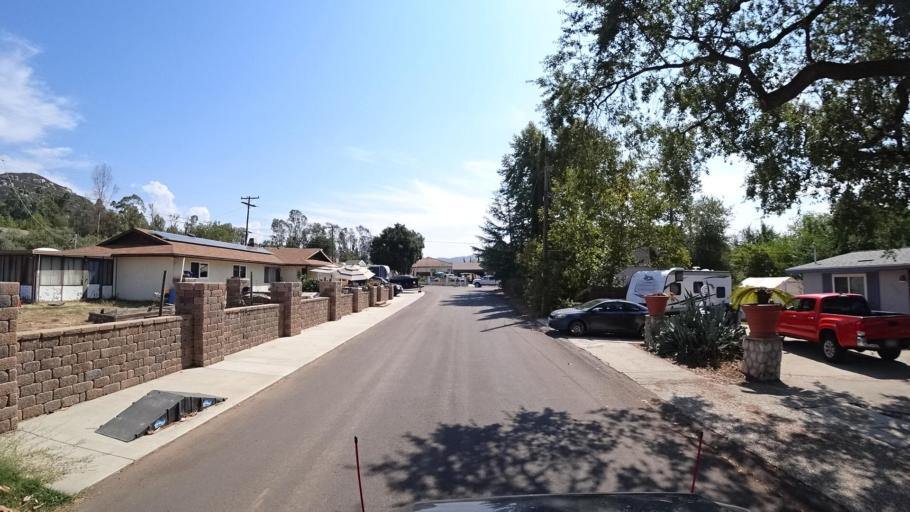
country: US
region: California
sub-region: San Diego County
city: Hidden Meadows
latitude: 33.1816
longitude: -117.1065
